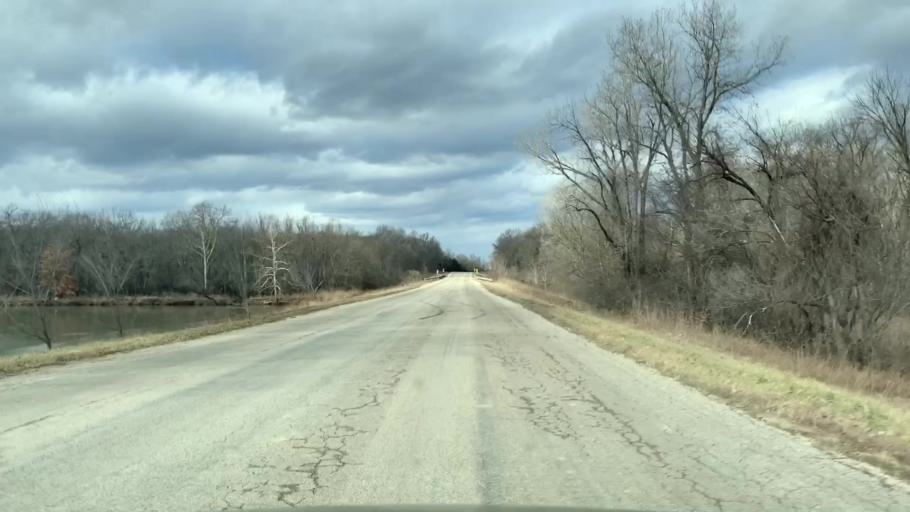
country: US
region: Kansas
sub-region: Allen County
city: Humboldt
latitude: 37.7514
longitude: -95.4707
